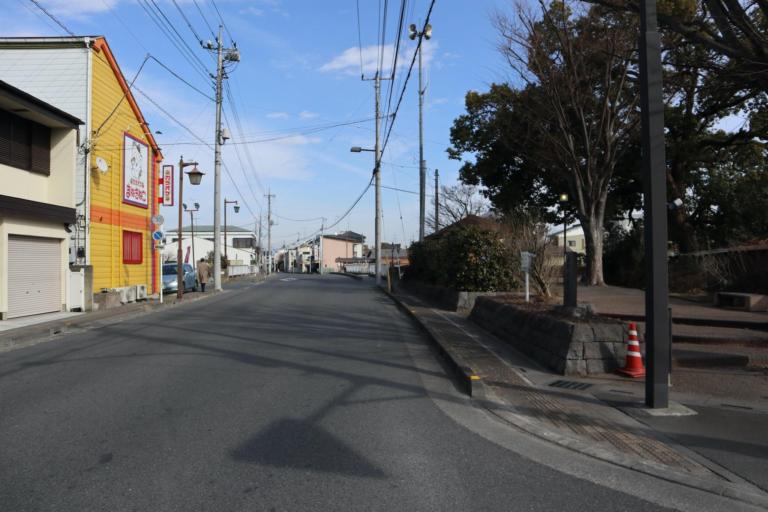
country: JP
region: Saitama
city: Gyoda
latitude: 36.1433
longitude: 139.4640
